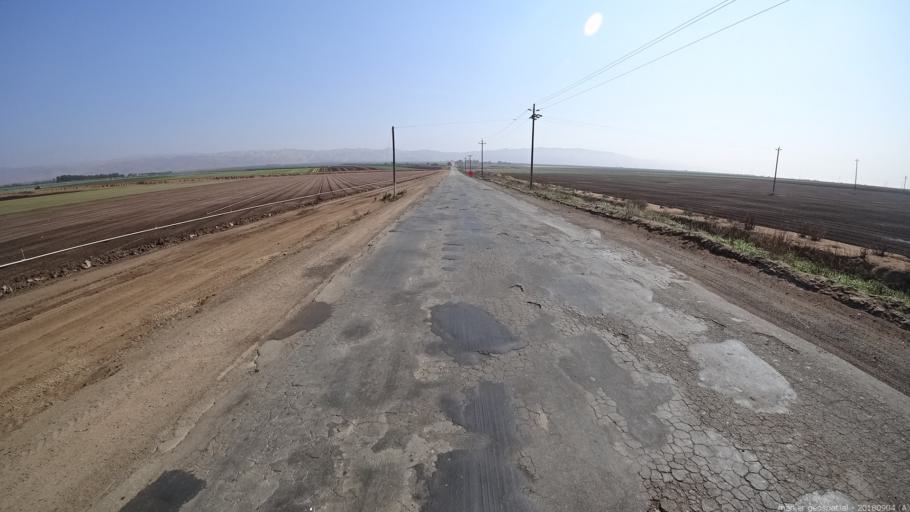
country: US
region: California
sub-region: Monterey County
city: Gonzales
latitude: 36.4956
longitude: -121.4218
